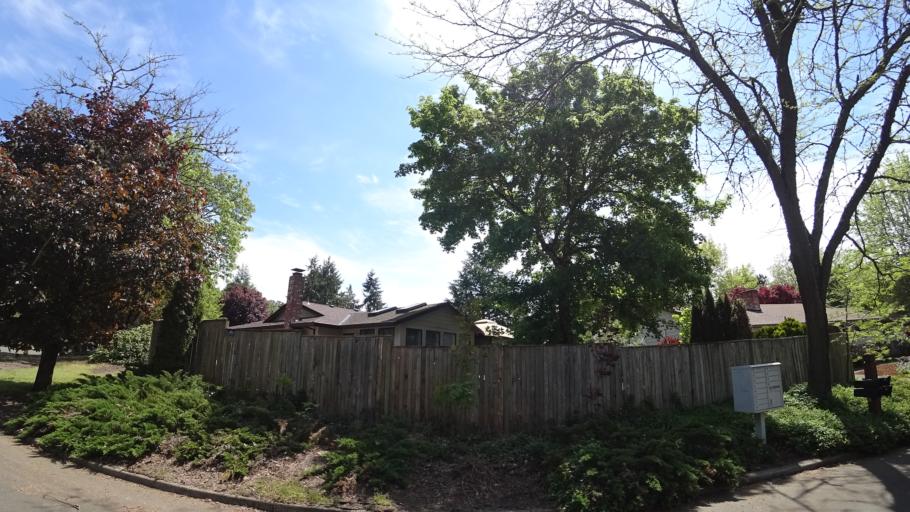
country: US
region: Oregon
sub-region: Washington County
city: Aloha
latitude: 45.4778
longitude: -122.8867
